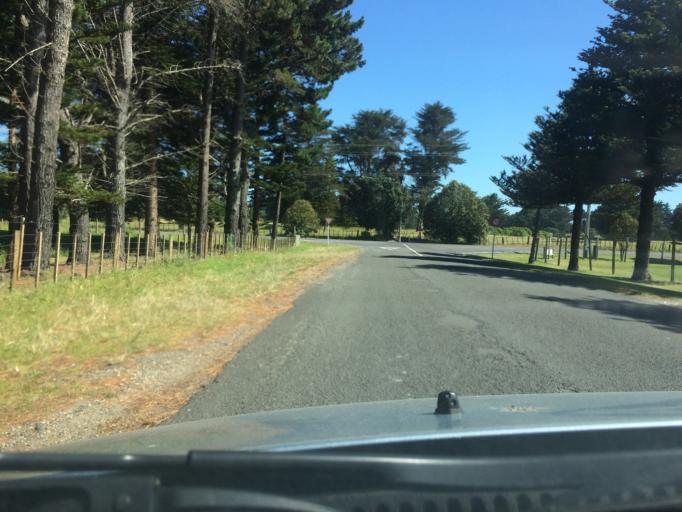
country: NZ
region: Gisborne
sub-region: Gisborne District
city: Gisborne
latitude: -38.6719
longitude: 177.9924
